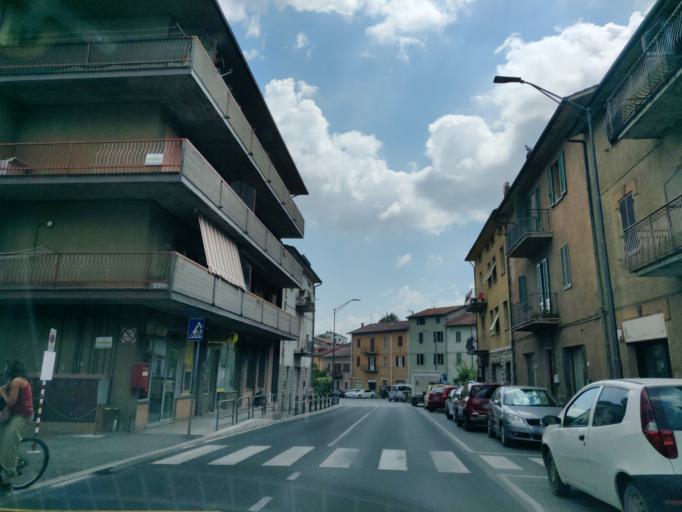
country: IT
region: Tuscany
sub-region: Provincia di Siena
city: Abbadia San Salvatore
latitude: 42.8785
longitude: 11.6770
